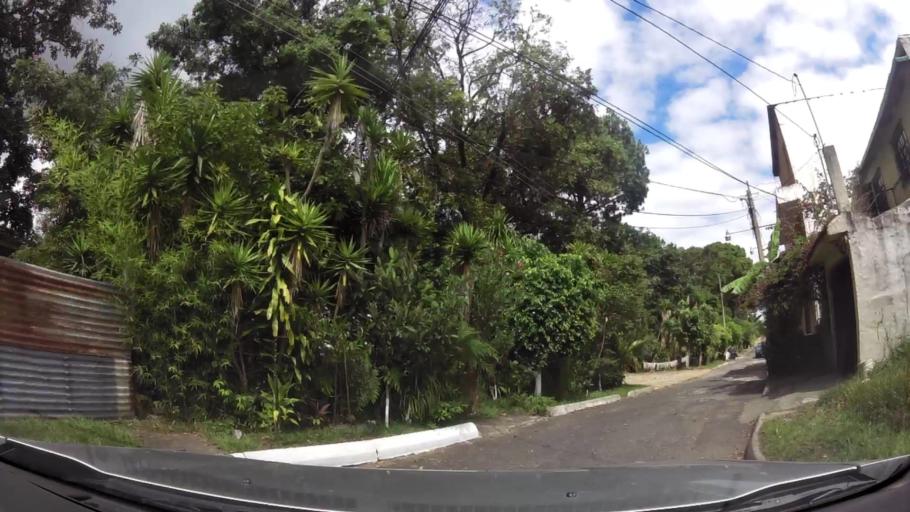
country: GT
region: Guatemala
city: Chinautla
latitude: 14.6876
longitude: -90.5514
